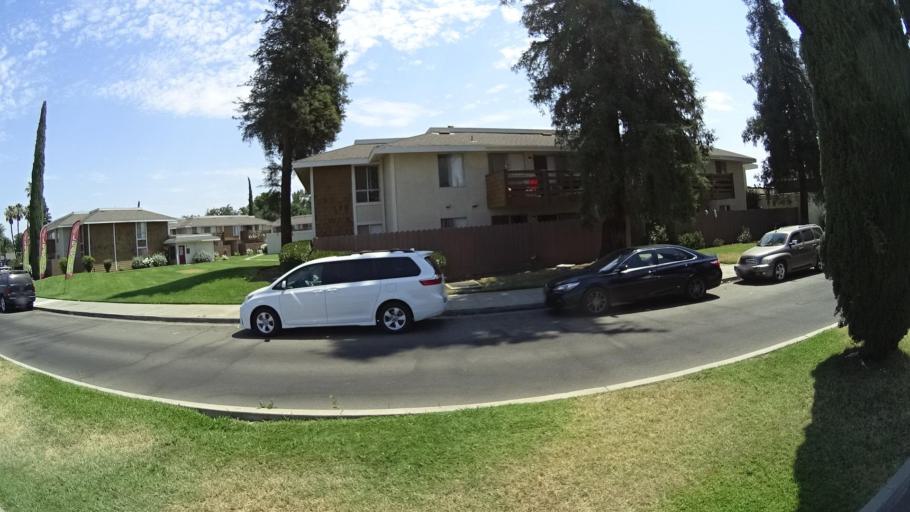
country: US
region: California
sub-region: Fresno County
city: Sunnyside
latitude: 36.7417
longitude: -119.6938
